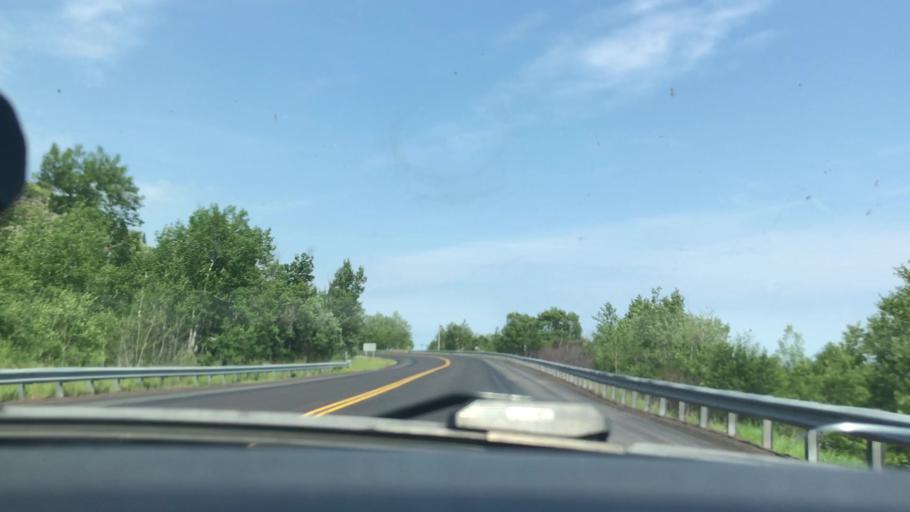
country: US
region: Minnesota
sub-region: Lake County
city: Silver Bay
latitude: 47.3769
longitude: -91.1615
